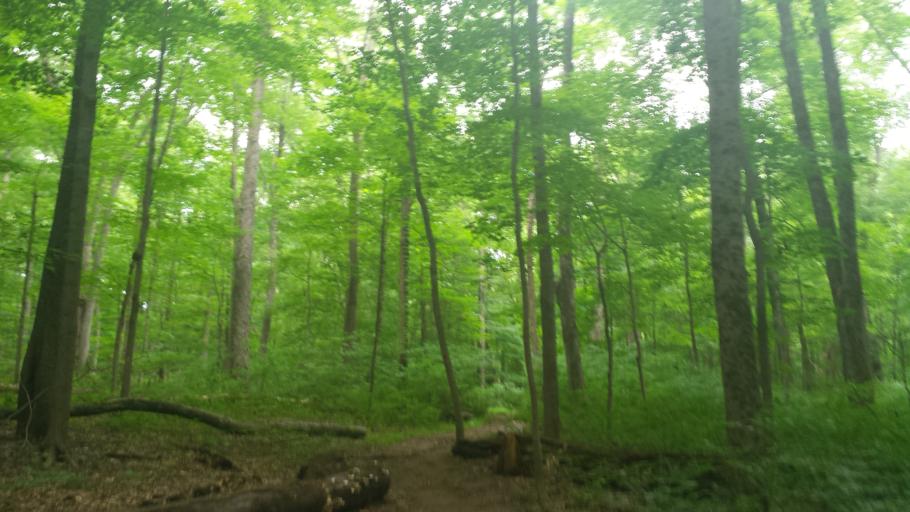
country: US
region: New York
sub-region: Westchester County
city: Yorktown Heights
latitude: 41.2226
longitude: -73.7839
